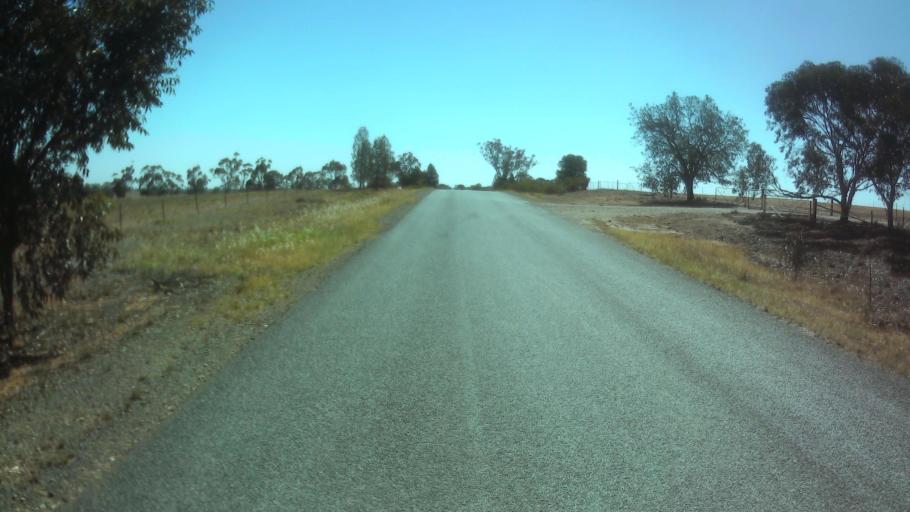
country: AU
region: New South Wales
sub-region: Weddin
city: Grenfell
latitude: -33.7539
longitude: 147.8385
